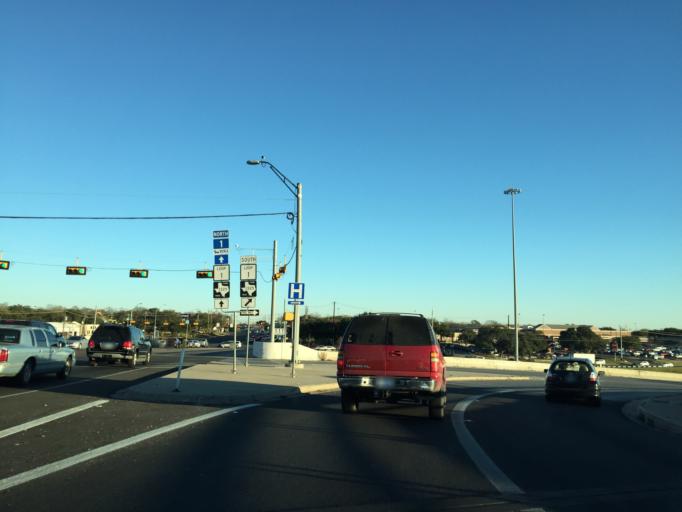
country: US
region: Texas
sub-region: Travis County
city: Wells Branch
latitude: 30.4207
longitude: -97.7050
